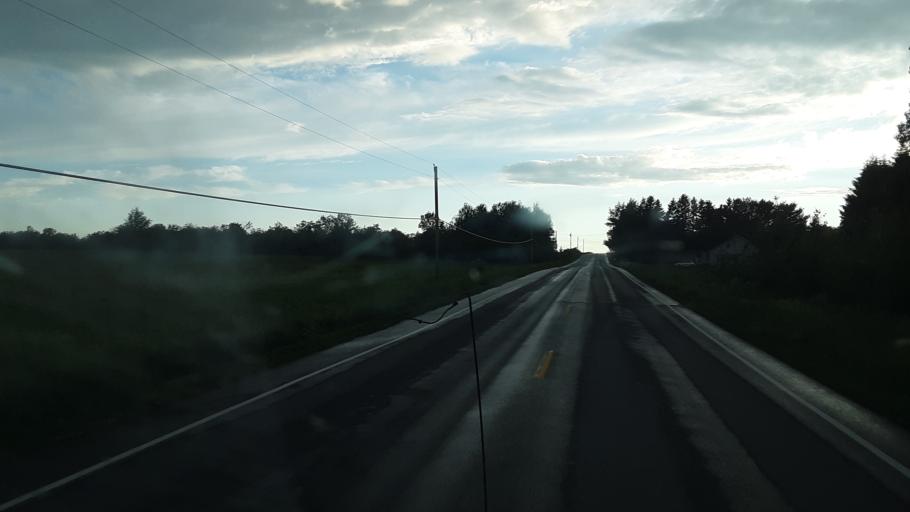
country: US
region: Maine
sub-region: Aroostook County
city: Easton
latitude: 46.6756
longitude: -67.9516
